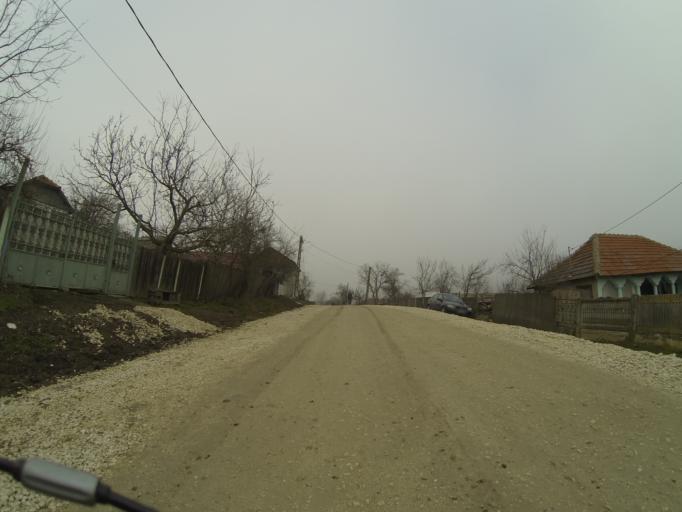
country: RO
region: Mehedinti
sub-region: Comuna Balacita
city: Gvardinita
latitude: 44.4030
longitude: 23.1454
